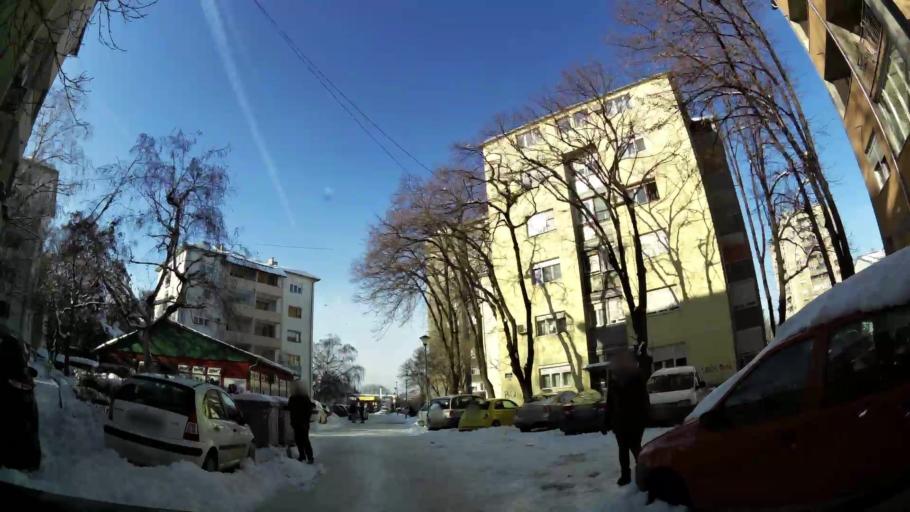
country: RS
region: Central Serbia
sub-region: Belgrade
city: Palilula
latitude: 44.8150
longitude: 20.5194
